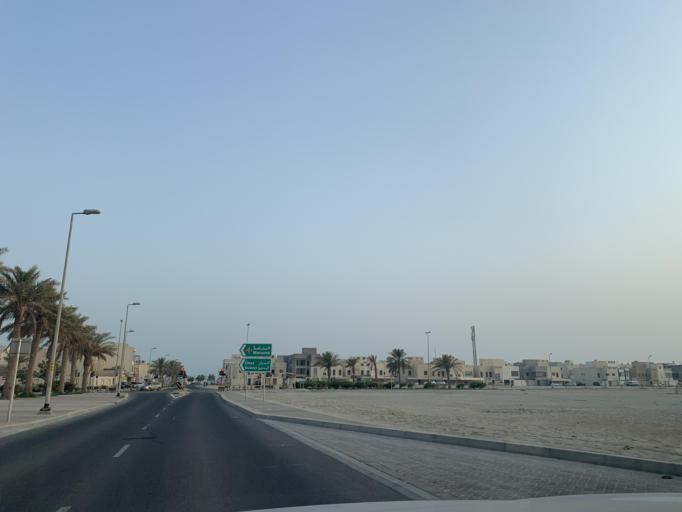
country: BH
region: Manama
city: Jidd Hafs
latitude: 26.2234
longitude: 50.4414
